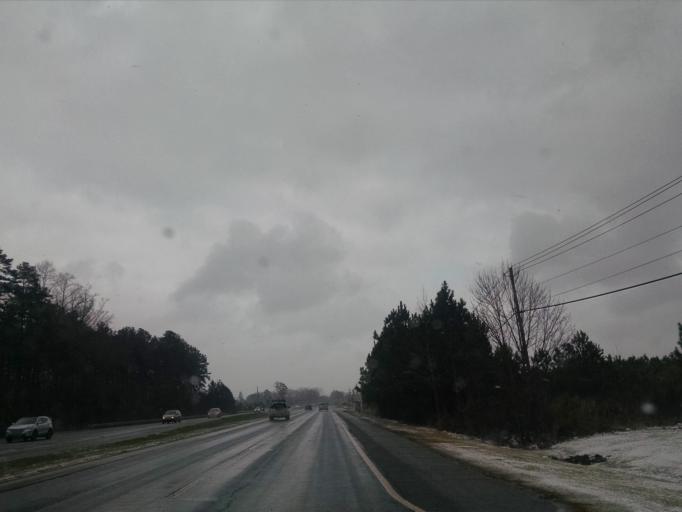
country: US
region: Georgia
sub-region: Gwinnett County
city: Suwanee
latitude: 34.0742
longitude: -84.0632
